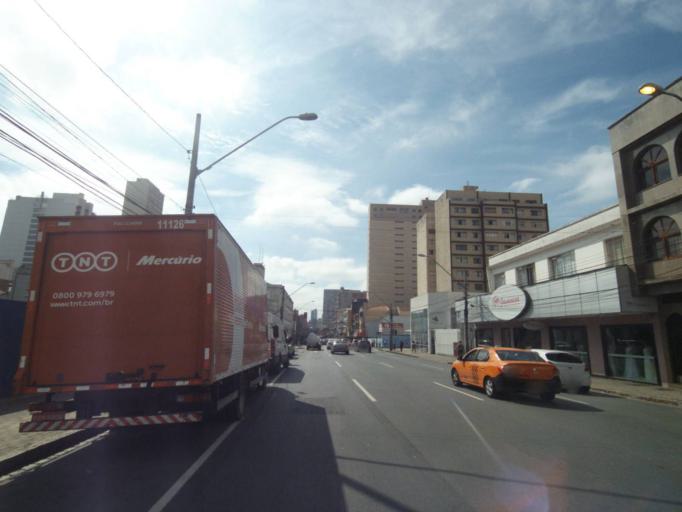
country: BR
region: Parana
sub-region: Curitiba
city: Curitiba
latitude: -25.4345
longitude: -49.2680
